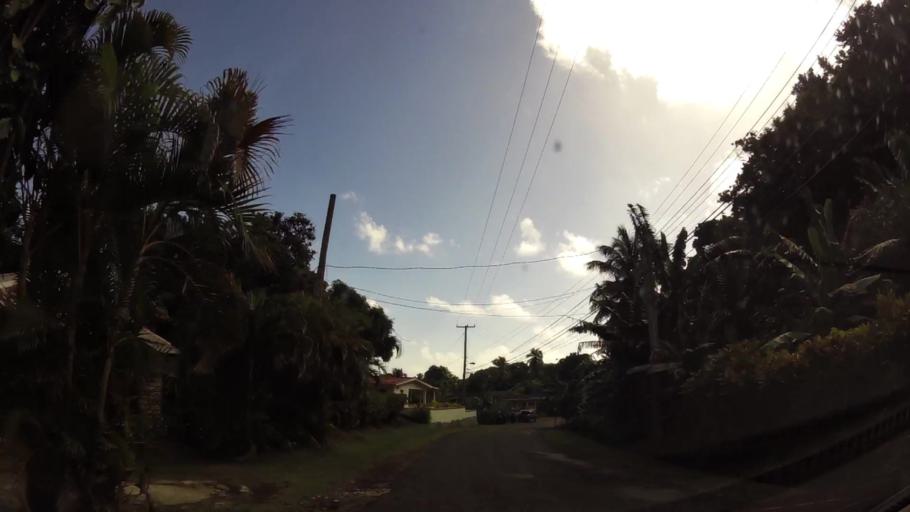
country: DM
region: Saint Andrew
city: Marigot
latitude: 15.5161
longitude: -61.2635
